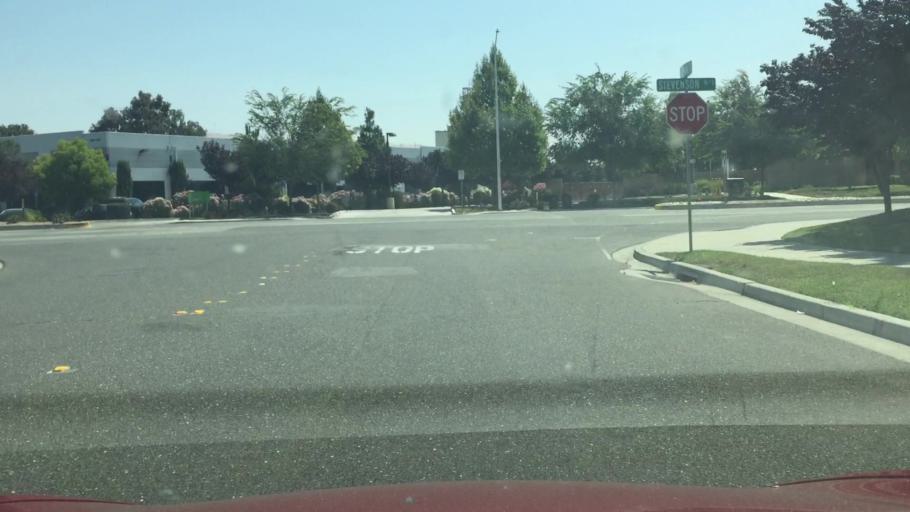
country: US
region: California
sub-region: Alameda County
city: Fremont
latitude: 37.5070
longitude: -121.9973
